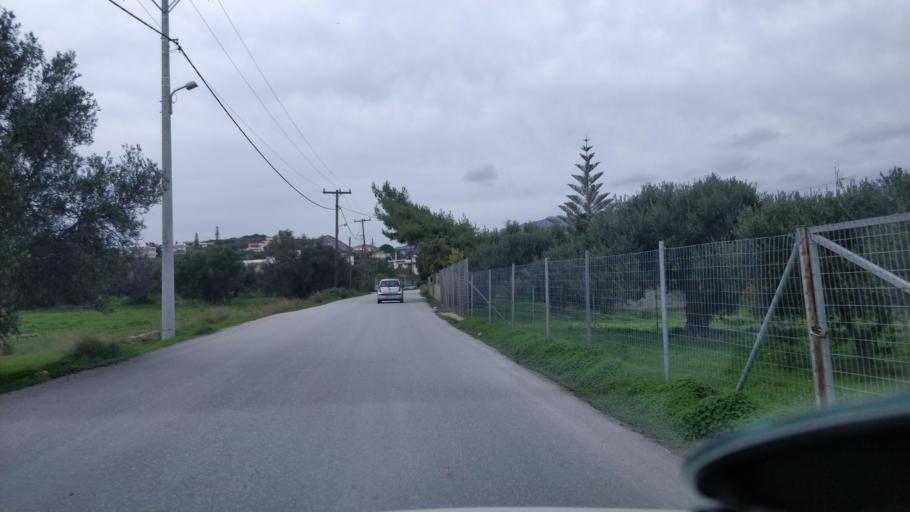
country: GR
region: Crete
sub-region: Nomos Lasithiou
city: Ierapetra
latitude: 35.0185
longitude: 25.7400
